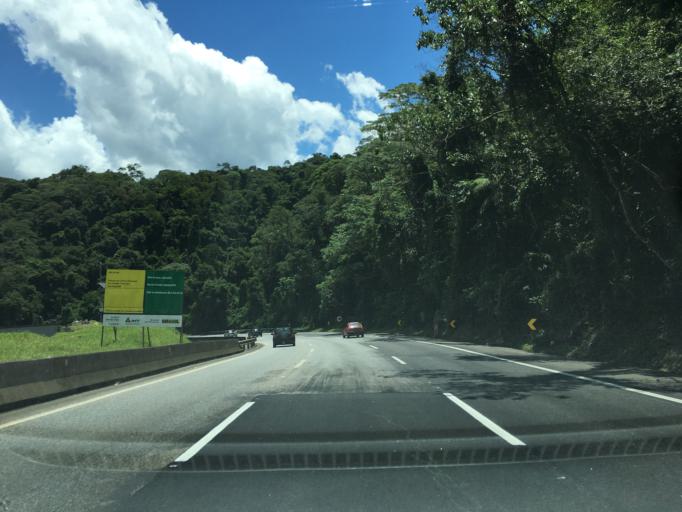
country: BR
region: Sao Paulo
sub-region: Mairipora
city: Mairipora
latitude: -23.3861
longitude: -46.5678
